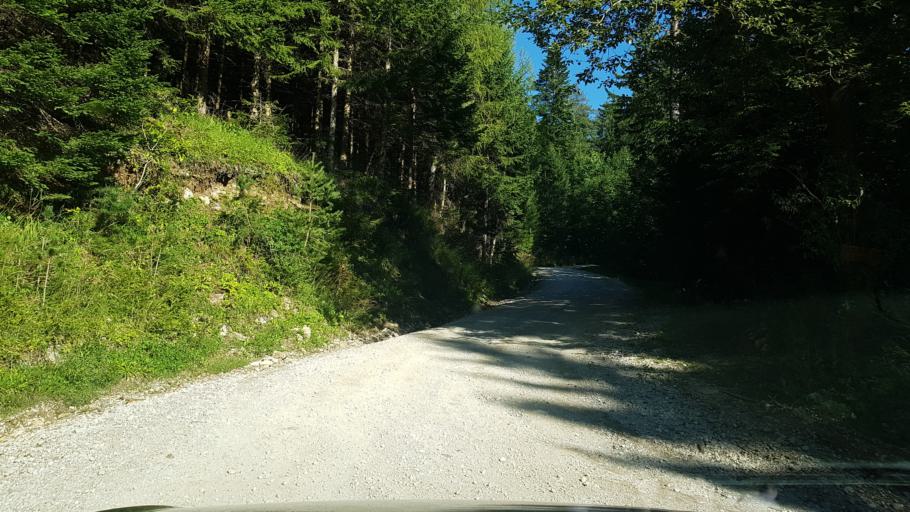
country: SI
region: Ravne na Koroskem
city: Kotlje
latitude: 46.4798
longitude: 14.9496
